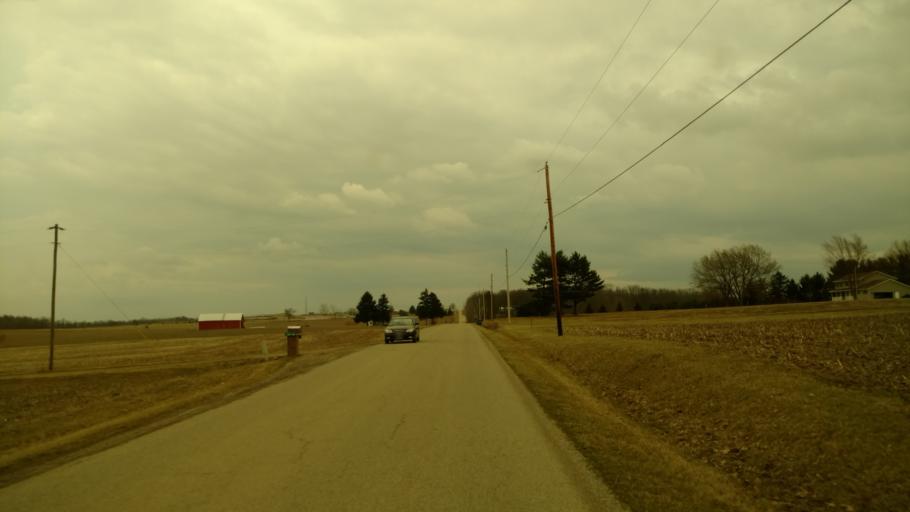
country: US
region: Ohio
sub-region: Richland County
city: Lexington
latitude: 40.6809
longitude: -82.6540
